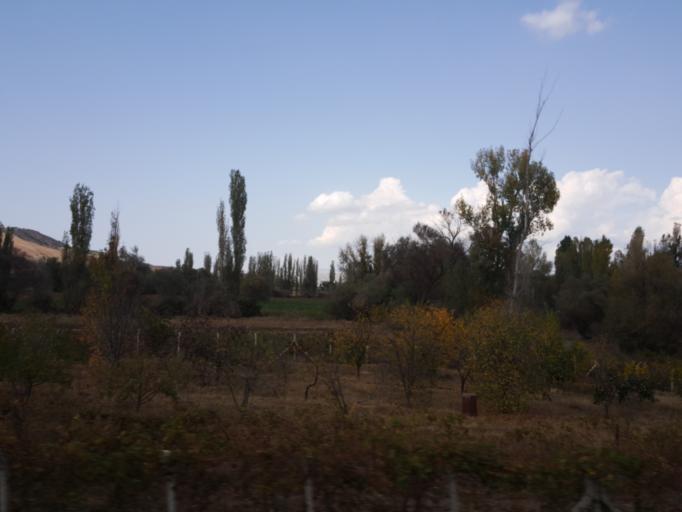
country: TR
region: Corum
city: Bogazkale
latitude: 40.1280
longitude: 34.5348
